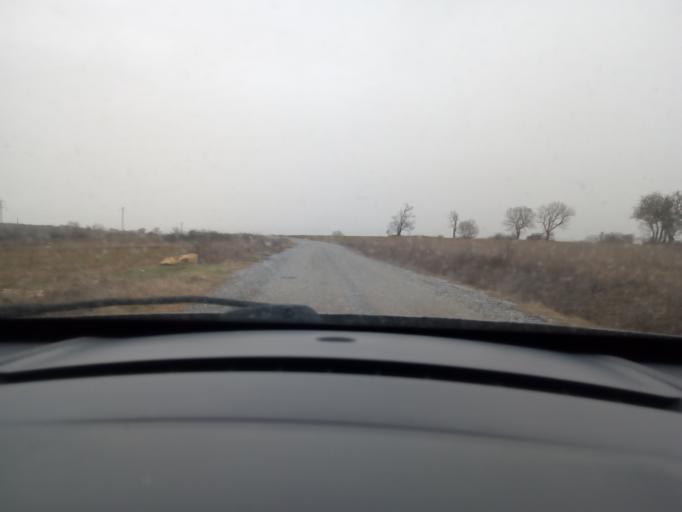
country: TR
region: Balikesir
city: Omerkoy
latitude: 39.8881
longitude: 28.0271
